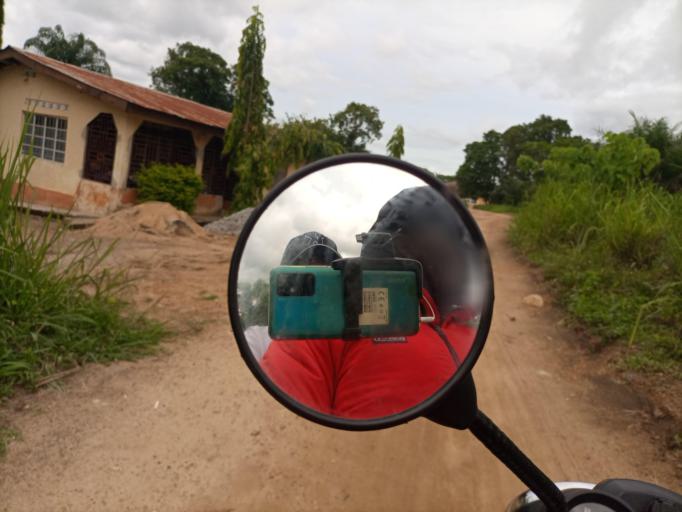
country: SL
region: Southern Province
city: Bo
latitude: 7.9720
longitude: -11.7245
